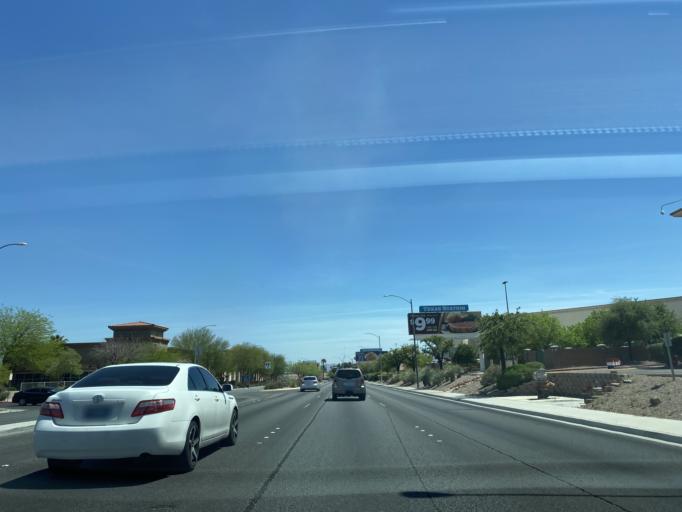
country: US
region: Nevada
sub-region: Clark County
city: Las Vegas
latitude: 36.1990
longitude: -115.1913
